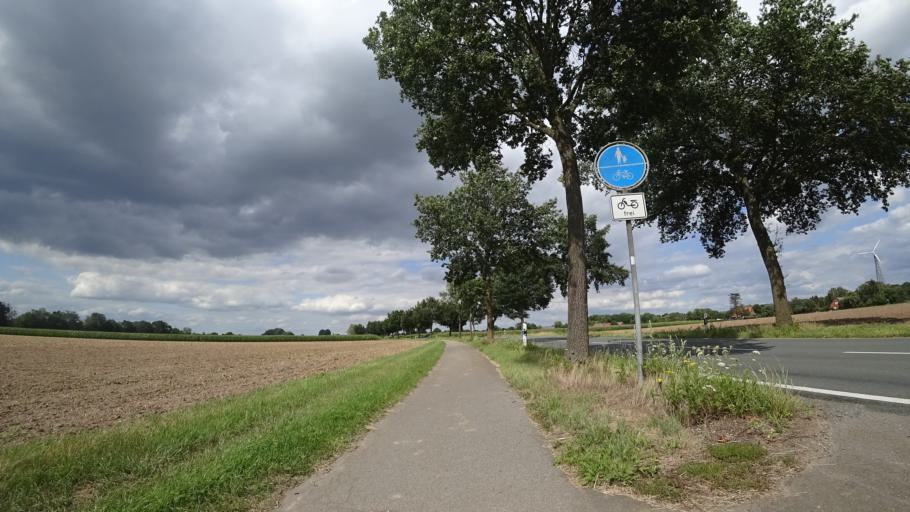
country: DE
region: Lower Saxony
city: Raddestorf
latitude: 52.4222
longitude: 9.0344
